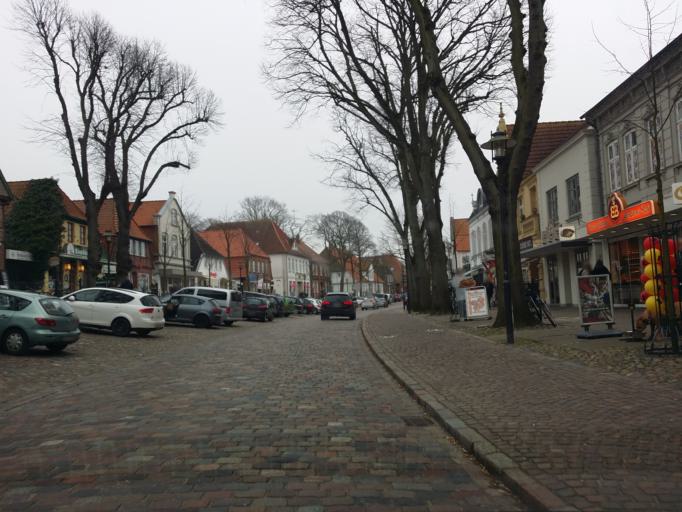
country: DE
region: Schleswig-Holstein
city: Fehmarn
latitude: 54.4387
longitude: 11.1976
